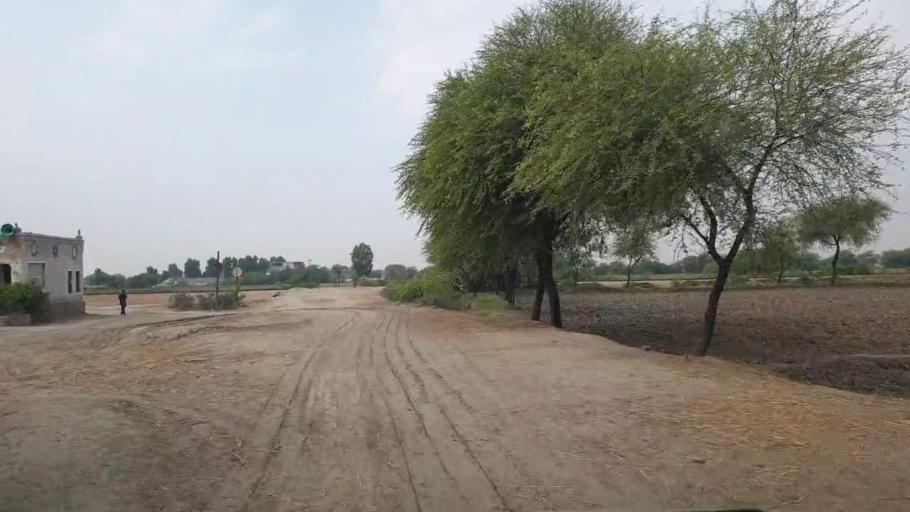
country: PK
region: Sindh
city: Talhar
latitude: 24.8635
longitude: 68.8191
